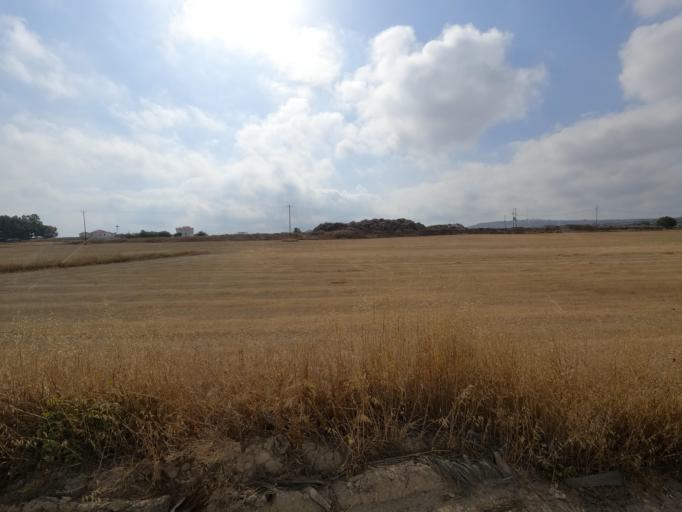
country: CY
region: Ammochostos
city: Paralimni
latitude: 35.0235
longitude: 34.0069
